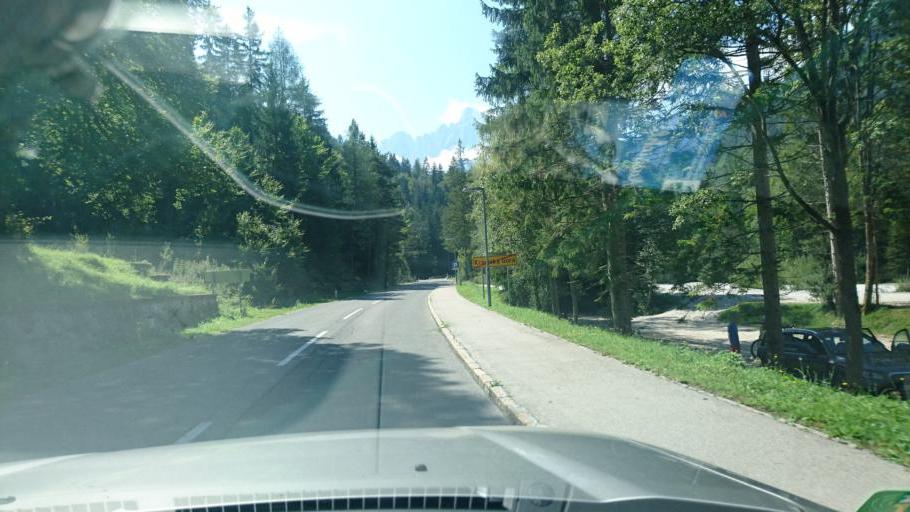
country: SI
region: Kranjska Gora
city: Kranjska Gora
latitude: 46.4713
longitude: 13.7850
